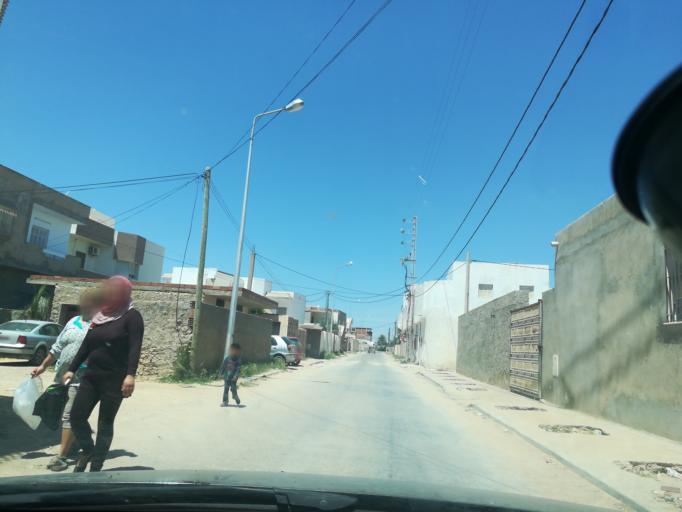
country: TN
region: Safaqis
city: Al Qarmadah
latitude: 34.8182
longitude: 10.7558
